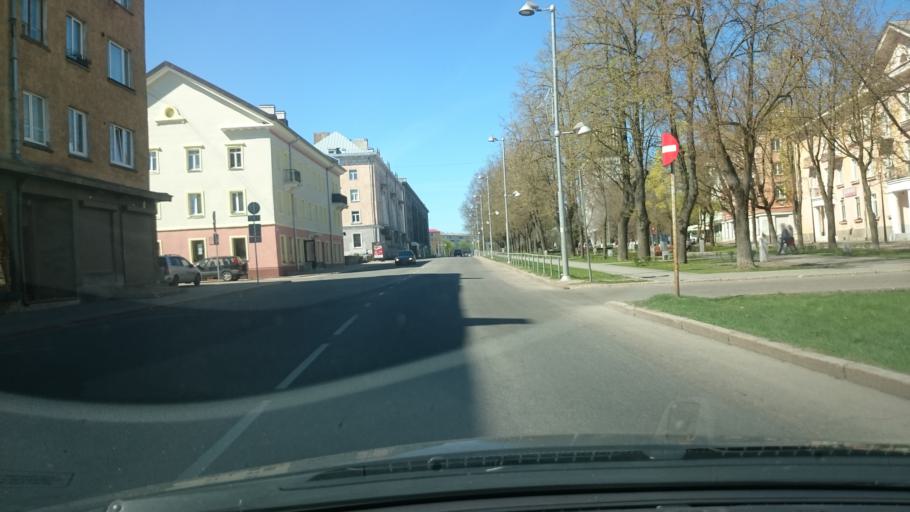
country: EE
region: Ida-Virumaa
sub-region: Narva linn
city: Narva
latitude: 59.3741
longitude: 28.1951
